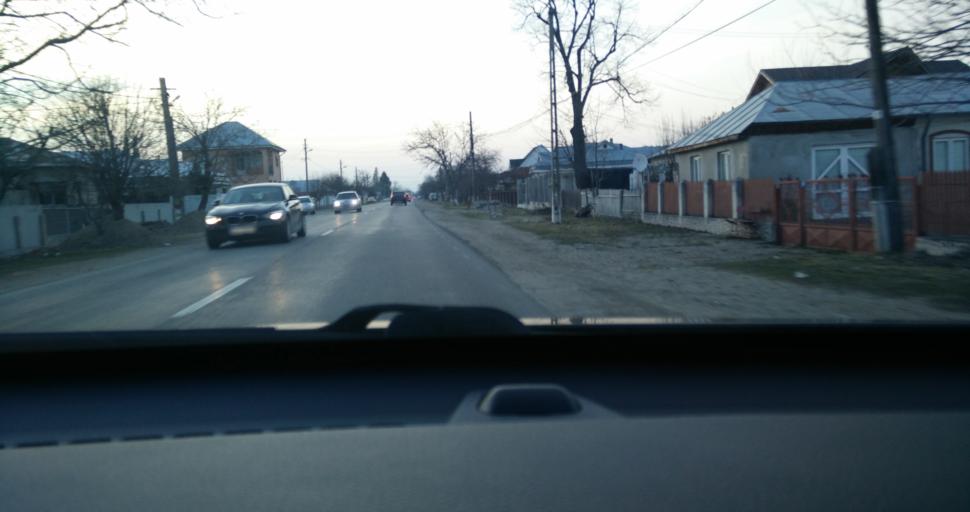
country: RO
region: Vrancea
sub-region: Comuna Rastoaca
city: Rastoaca
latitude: 45.6642
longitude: 27.2746
